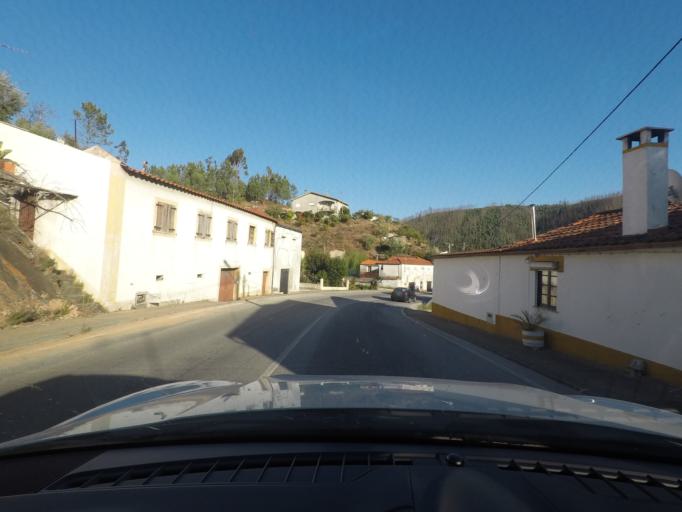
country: PT
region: Coimbra
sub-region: Vila Nova de Poiares
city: Poiares
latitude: 40.1718
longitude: -8.3201
